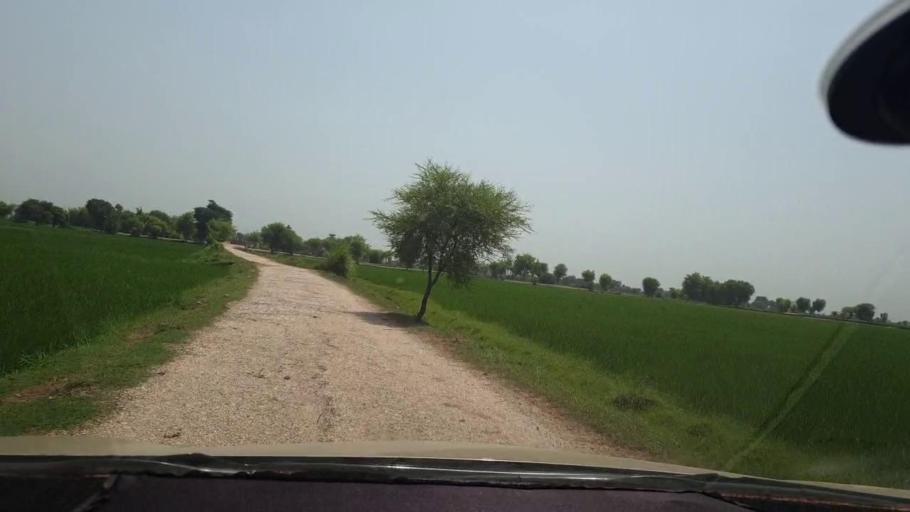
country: PK
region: Sindh
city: Kambar
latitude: 27.6401
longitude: 67.9328
